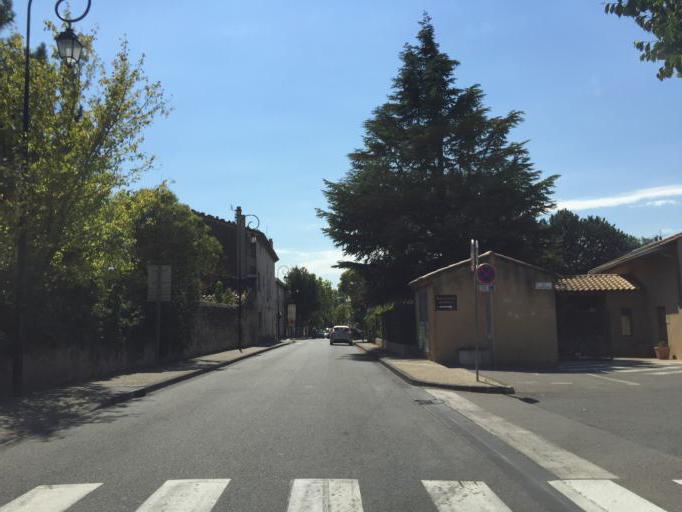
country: FR
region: Provence-Alpes-Cote d'Azur
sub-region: Departement du Vaucluse
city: Pernes-les-Fontaines
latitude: 44.0010
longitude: 5.0593
